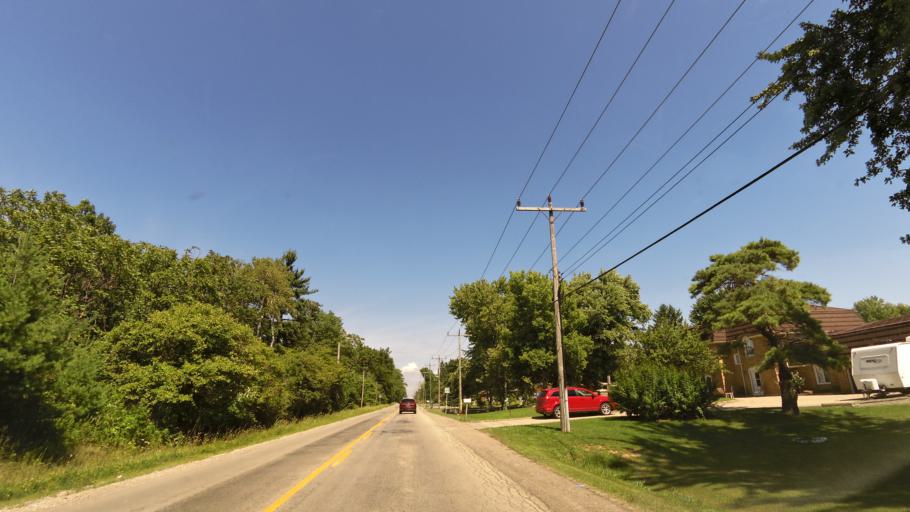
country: CA
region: Ontario
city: Ancaster
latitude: 43.1917
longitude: -79.9357
